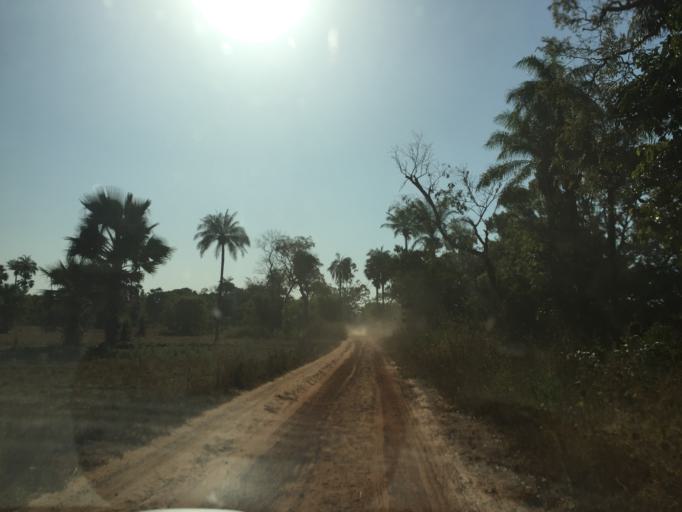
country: GW
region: Oio
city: Farim
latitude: 12.4615
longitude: -15.3001
